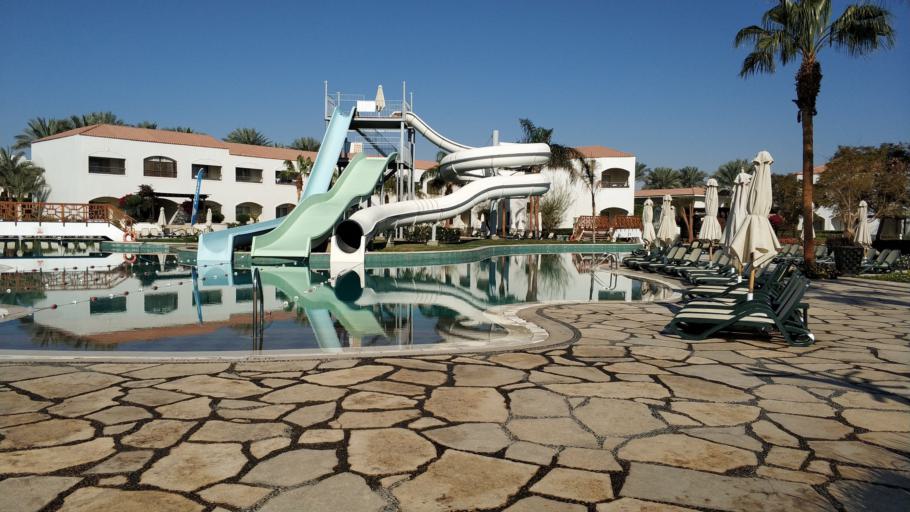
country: EG
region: South Sinai
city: Sharm el-Sheikh
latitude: 27.9198
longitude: 34.3611
